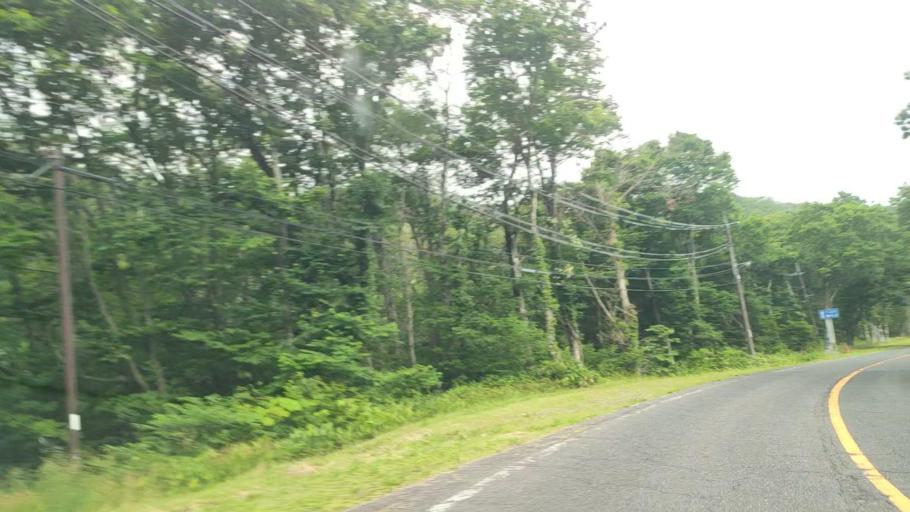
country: JP
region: Tottori
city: Yonago
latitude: 35.3369
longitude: 133.5565
